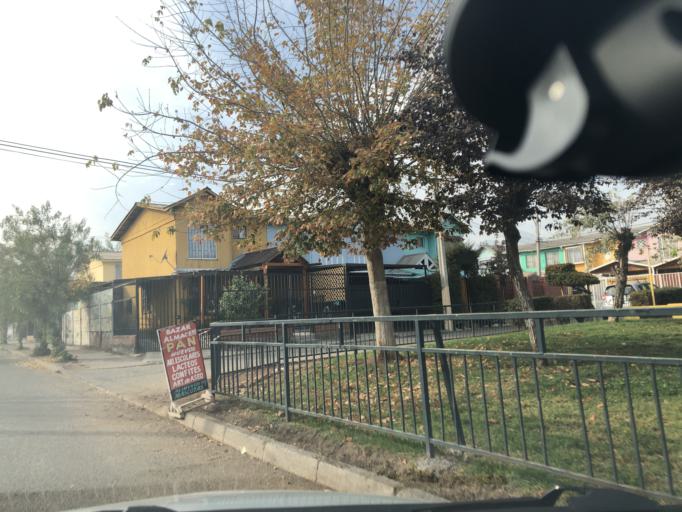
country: CL
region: Santiago Metropolitan
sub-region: Provincia de Cordillera
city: Puente Alto
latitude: -33.5819
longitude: -70.5566
